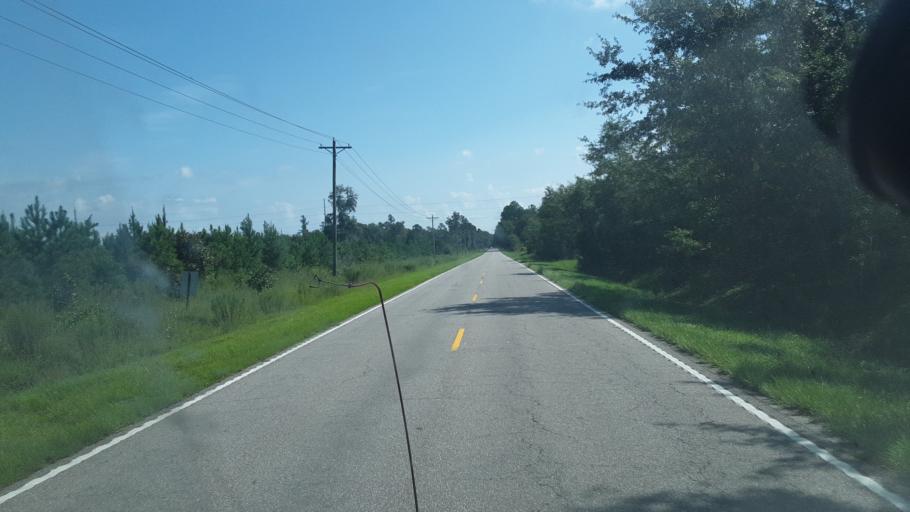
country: US
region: South Carolina
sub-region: Hampton County
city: Varnville
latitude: 32.8799
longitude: -81.0343
